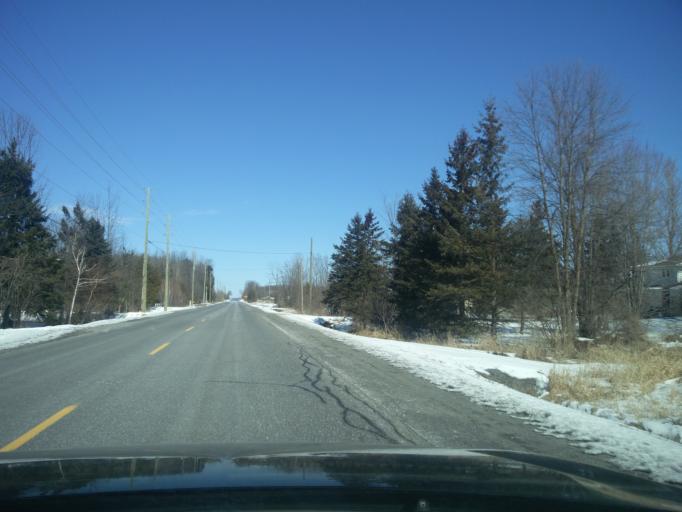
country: CA
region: Ontario
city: Bells Corners
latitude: 45.2302
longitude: -75.7226
